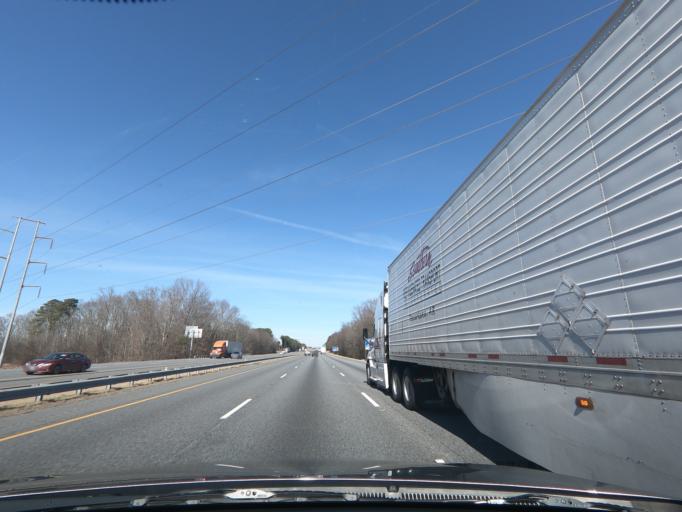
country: US
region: Georgia
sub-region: Gordon County
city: Calhoun
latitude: 34.4548
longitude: -84.9194
